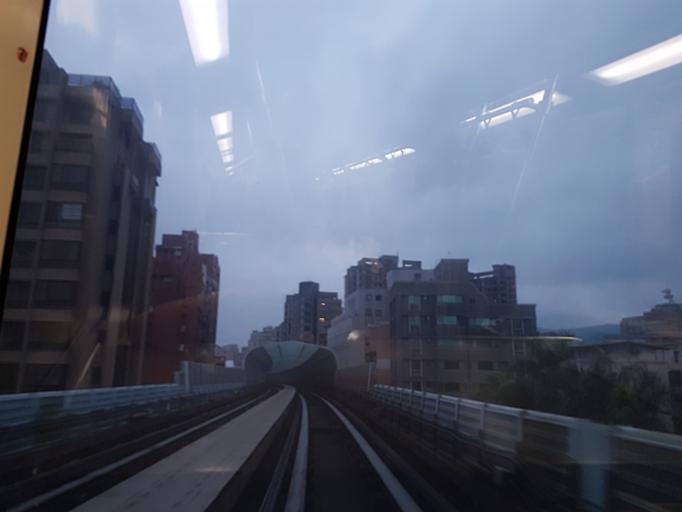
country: TW
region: Taipei
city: Taipei
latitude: 25.0709
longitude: 121.6107
